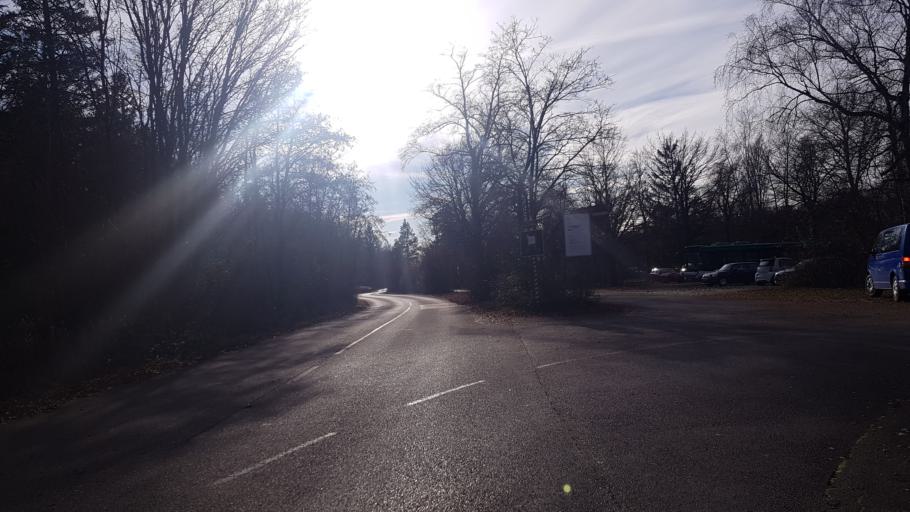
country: DE
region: Bavaria
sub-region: Upper Bavaria
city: Oberschleissheim
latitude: 48.2495
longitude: 11.5277
